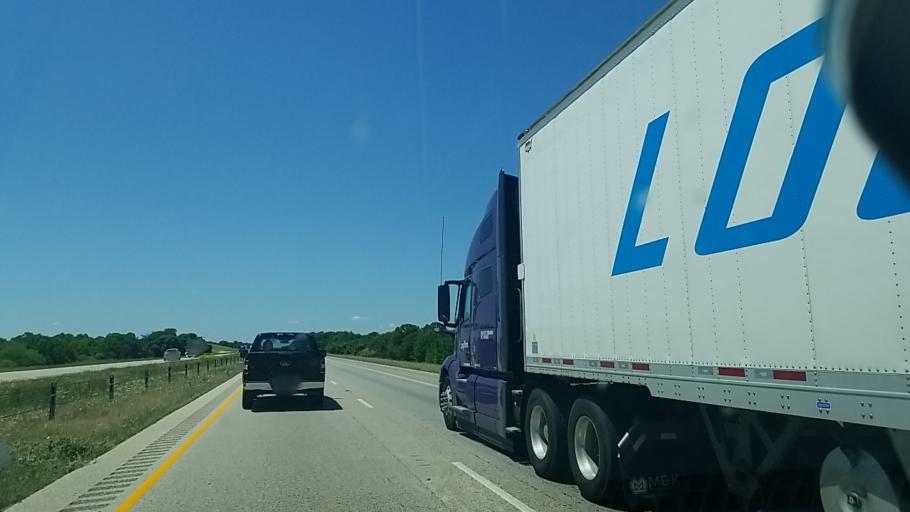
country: US
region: Texas
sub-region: Leon County
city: Buffalo
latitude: 31.4301
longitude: -96.0571
